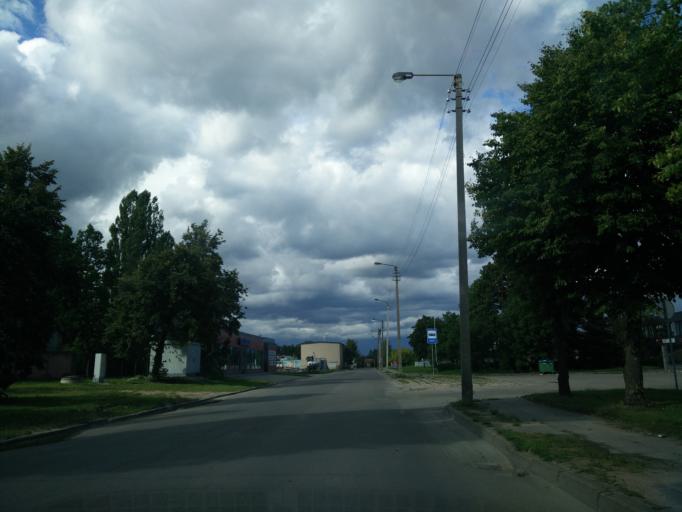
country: LT
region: Kauno apskritis
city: Dainava (Kaunas)
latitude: 54.9093
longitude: 24.0097
